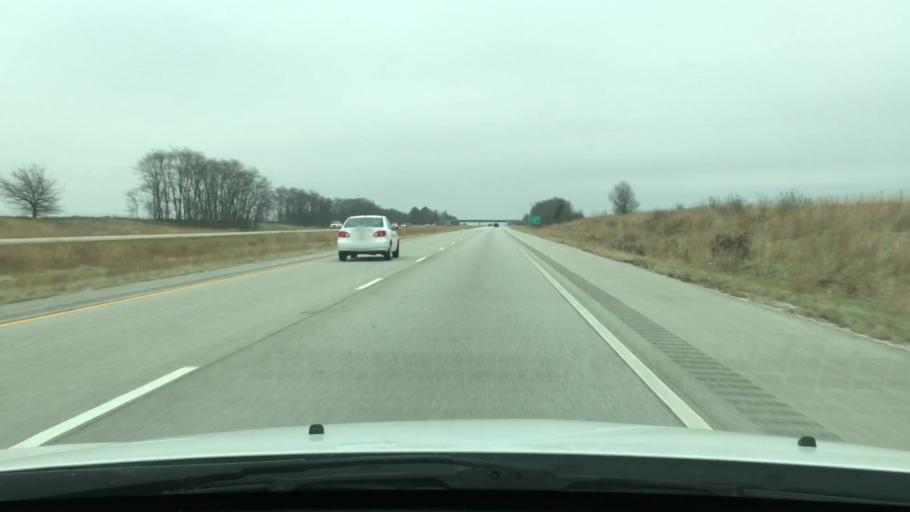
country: US
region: Illinois
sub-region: Sangamon County
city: New Berlin
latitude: 39.7400
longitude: -89.9351
